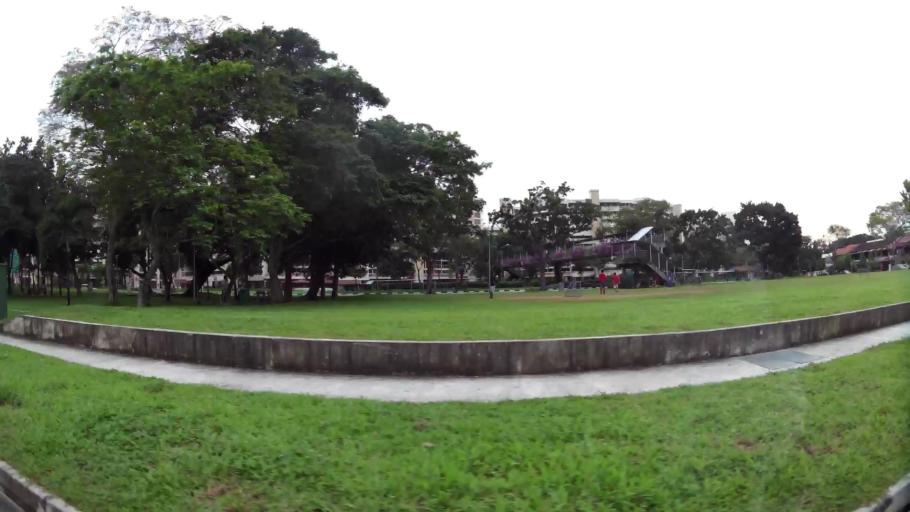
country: SG
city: Singapore
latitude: 1.3677
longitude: 103.8896
